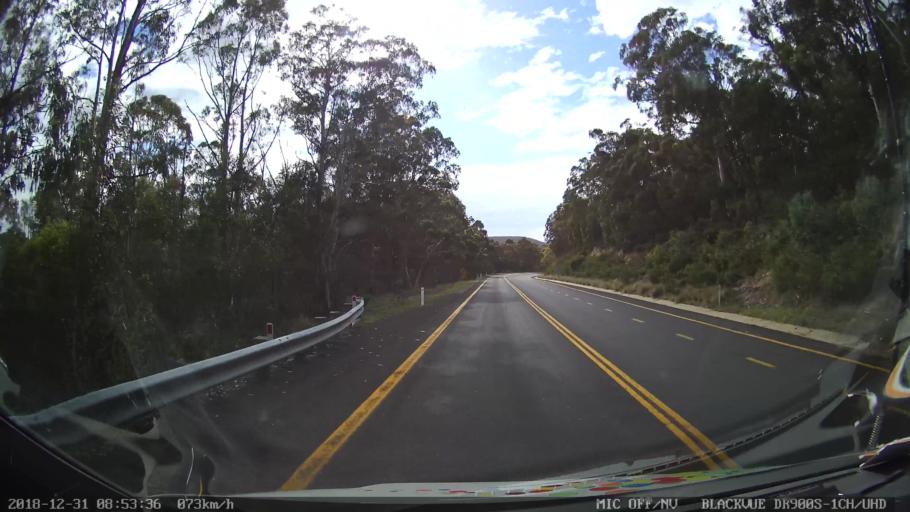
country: AU
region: New South Wales
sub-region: Snowy River
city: Jindabyne
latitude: -36.3494
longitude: 148.5507
